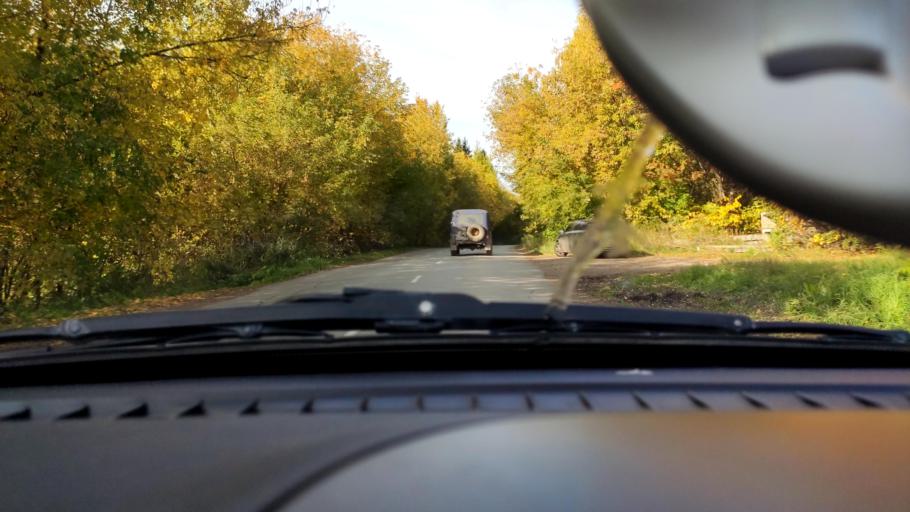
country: RU
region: Perm
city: Overyata
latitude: 58.0593
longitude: 55.8996
